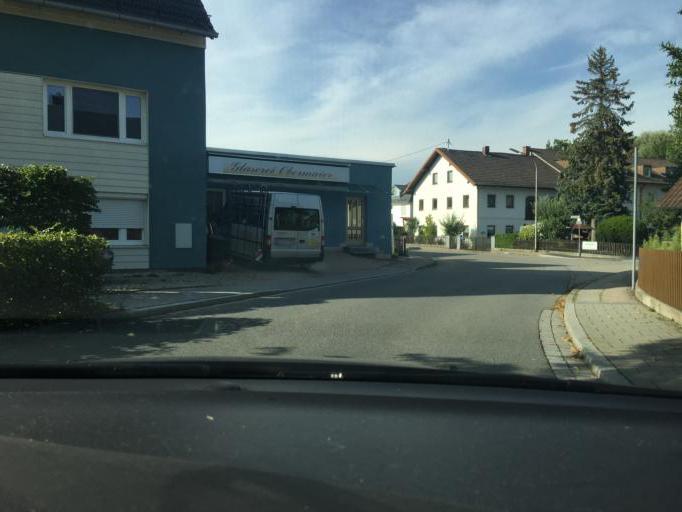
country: DE
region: Bavaria
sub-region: Upper Bavaria
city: Erding
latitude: 48.2937
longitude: 11.9071
